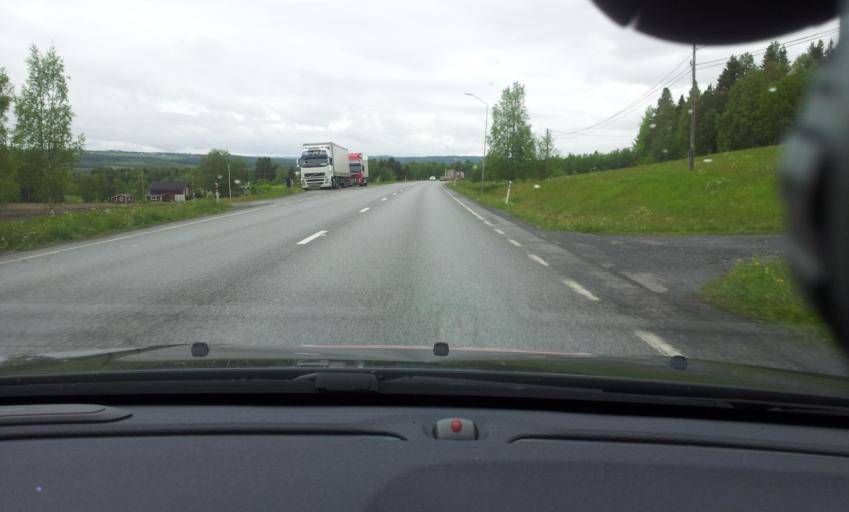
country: SE
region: Jaemtland
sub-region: Krokoms Kommun
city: Valla
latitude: 63.3193
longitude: 14.0753
